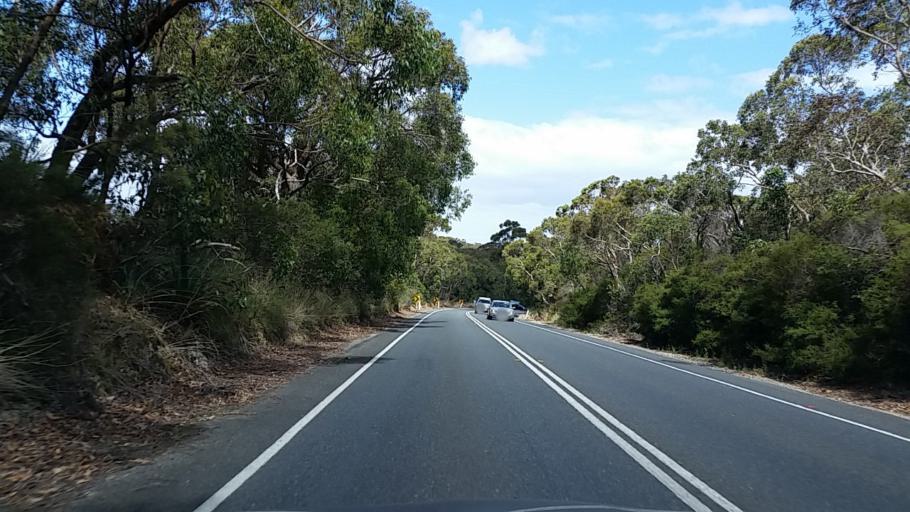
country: AU
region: South Australia
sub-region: Alexandrina
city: Port Elliot
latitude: -35.4609
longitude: 138.6475
